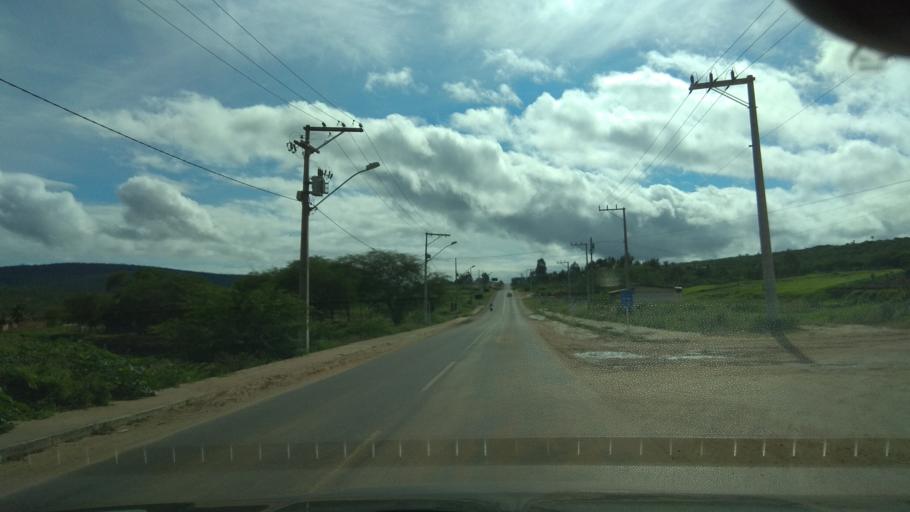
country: BR
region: Bahia
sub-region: Jaguaquara
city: Jaguaquara
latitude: -13.4468
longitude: -39.9371
